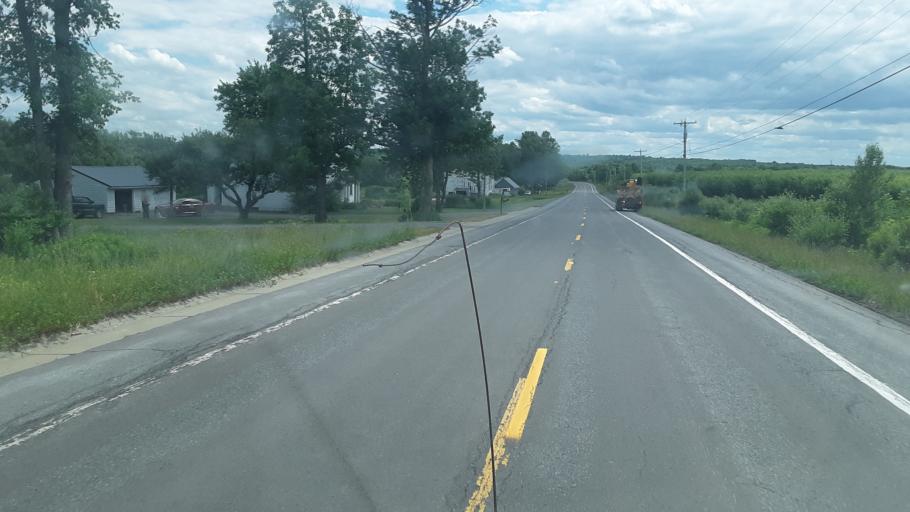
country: US
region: New York
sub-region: Oneida County
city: Rome
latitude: 43.3836
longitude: -75.4874
